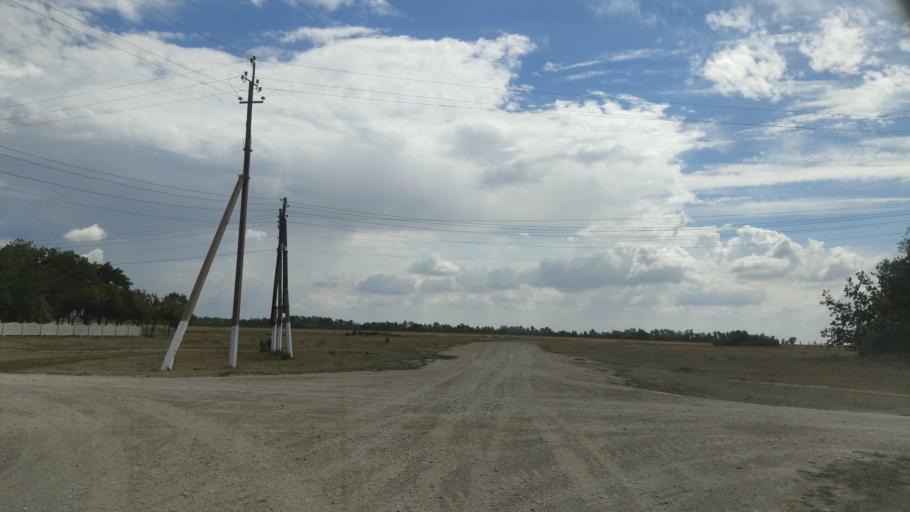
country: KZ
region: Pavlodar
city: Pavlodar
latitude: 52.6478
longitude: 77.0244
